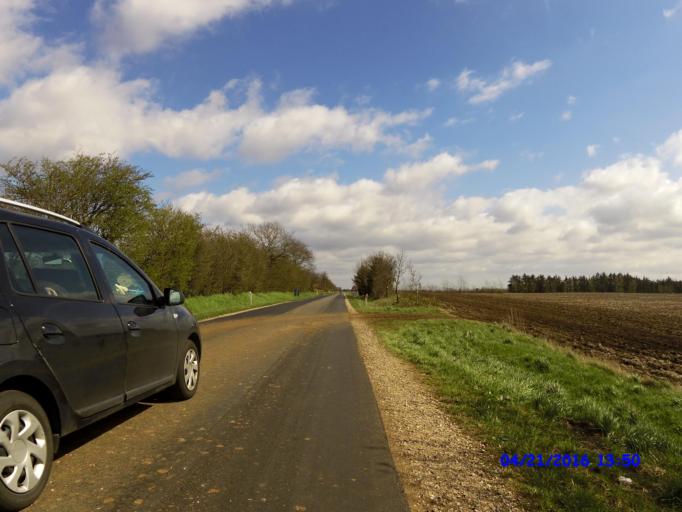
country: DK
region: South Denmark
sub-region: Haderslev Kommune
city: Gram
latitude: 55.2448
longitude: 8.9967
